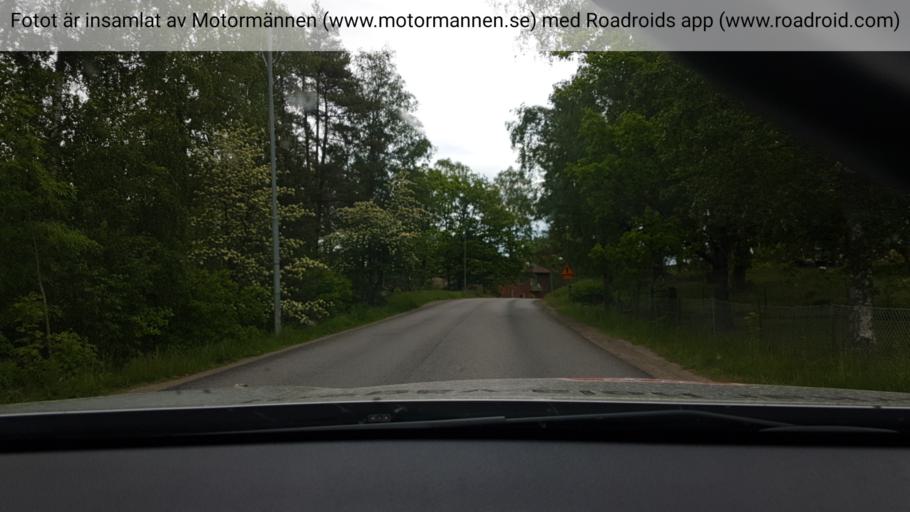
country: SE
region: Stockholm
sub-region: Nynashamns Kommun
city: Osmo
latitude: 58.9824
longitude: 17.9000
